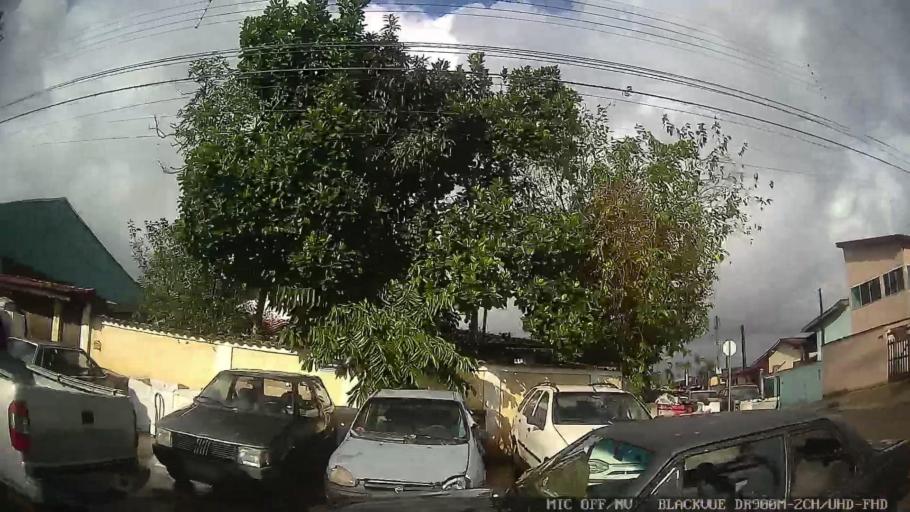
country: BR
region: Sao Paulo
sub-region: Itanhaem
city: Itanhaem
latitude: -24.2154
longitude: -46.8825
